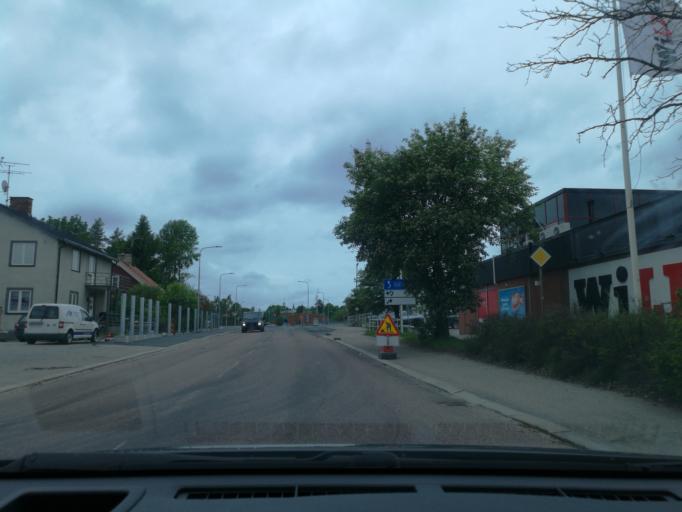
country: SE
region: Dalarna
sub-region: Ludvika Kommun
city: Ludvika
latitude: 60.1516
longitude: 15.1996
